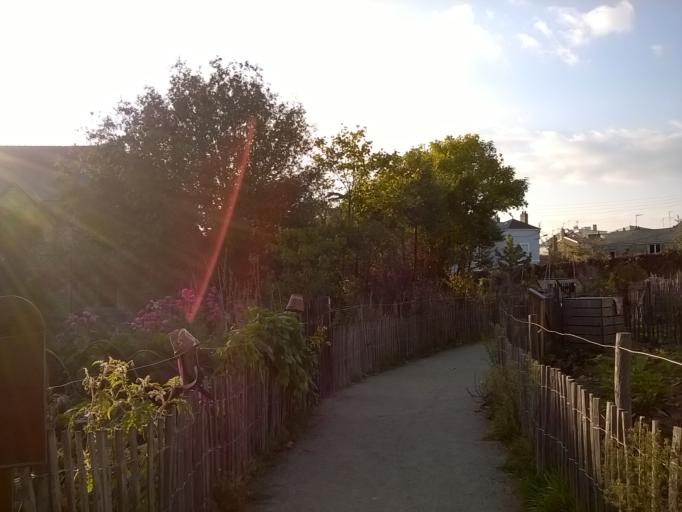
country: FR
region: Pays de la Loire
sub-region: Departement de la Loire-Atlantique
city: Nantes
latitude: 47.2005
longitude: -1.5853
